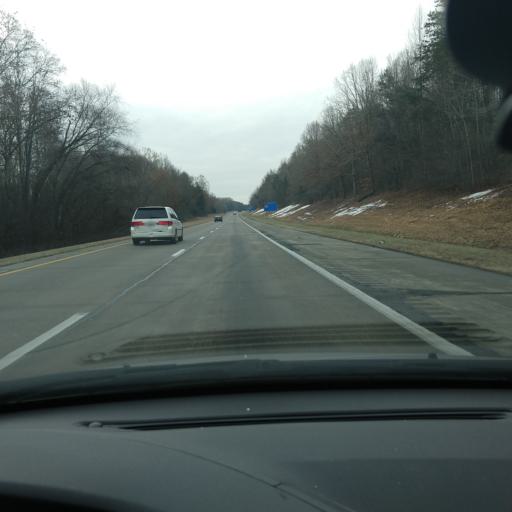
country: US
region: North Carolina
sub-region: Davidson County
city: Midway
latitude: 35.9821
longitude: -80.2344
